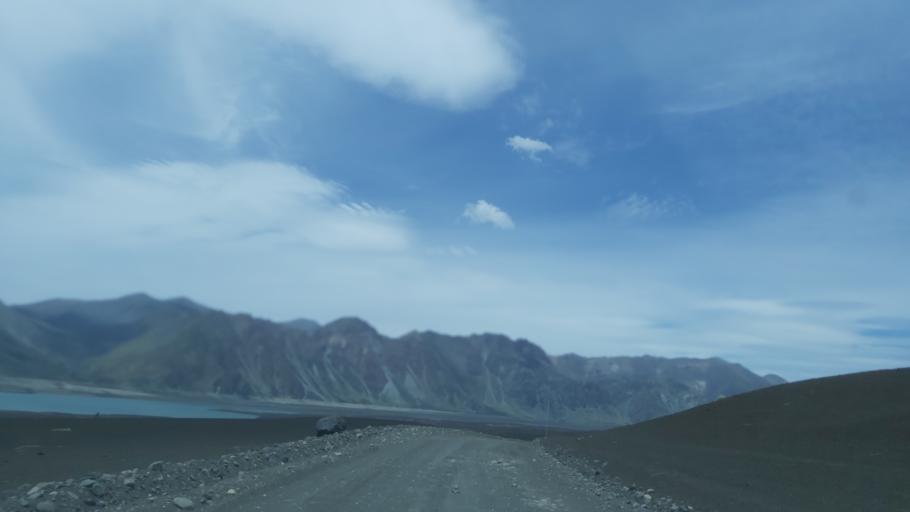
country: AR
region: Neuquen
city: Andacollo
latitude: -37.4207
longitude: -71.2885
